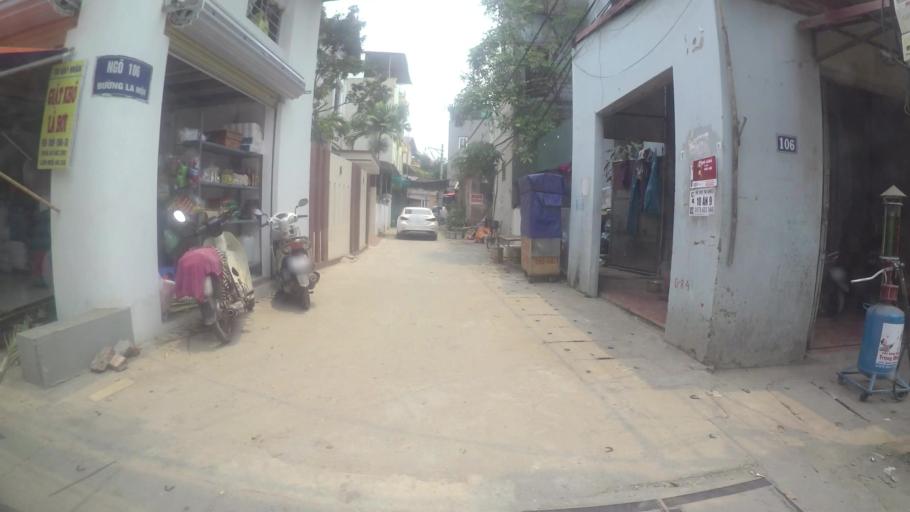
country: VN
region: Ha Noi
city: Ha Dong
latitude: 20.9814
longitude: 105.7487
